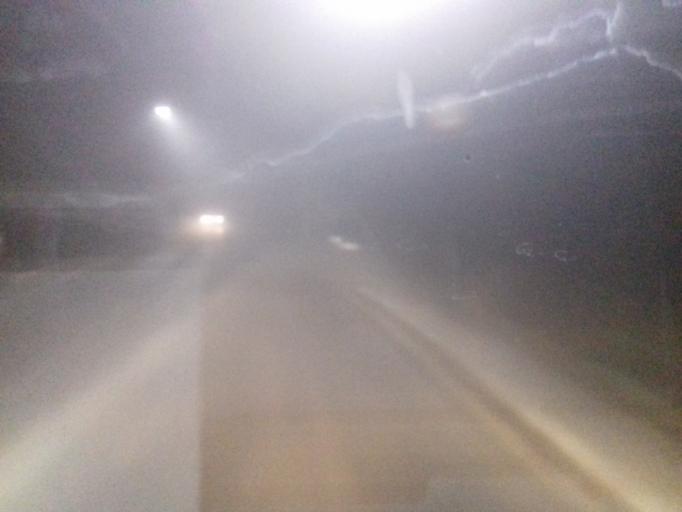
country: BA
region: Federation of Bosnia and Herzegovina
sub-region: Kanton Sarajevo
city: Sarajevo
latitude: 43.8321
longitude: 18.3197
